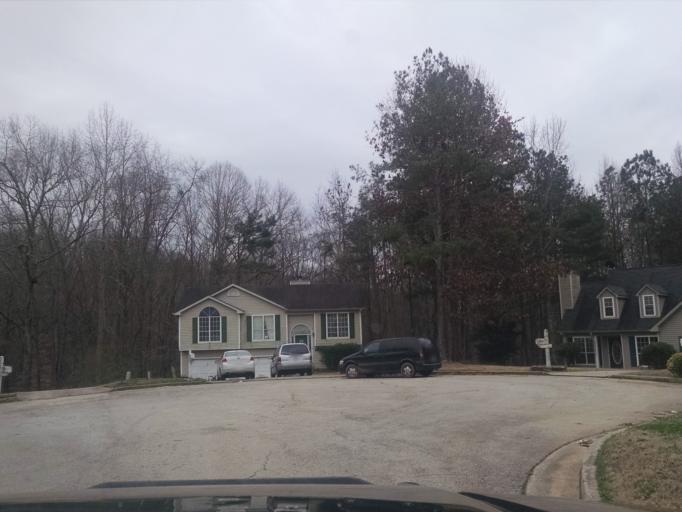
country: US
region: Georgia
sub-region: Hall County
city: Oakwood
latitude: 34.2019
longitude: -83.8648
